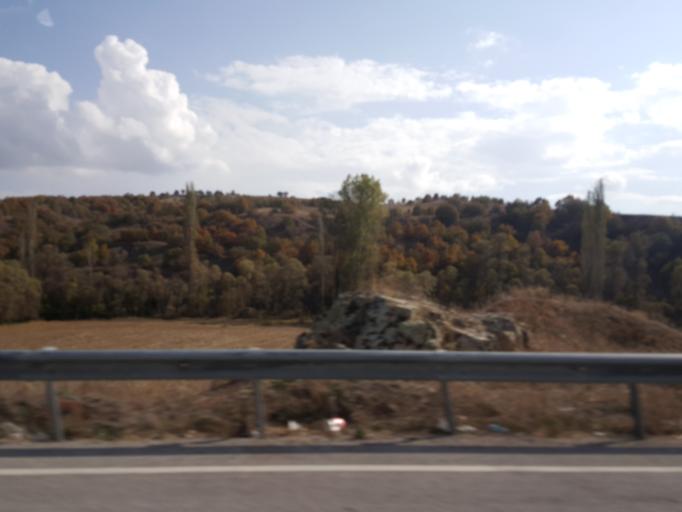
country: TR
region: Corum
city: Alaca
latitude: 40.3166
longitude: 34.6743
